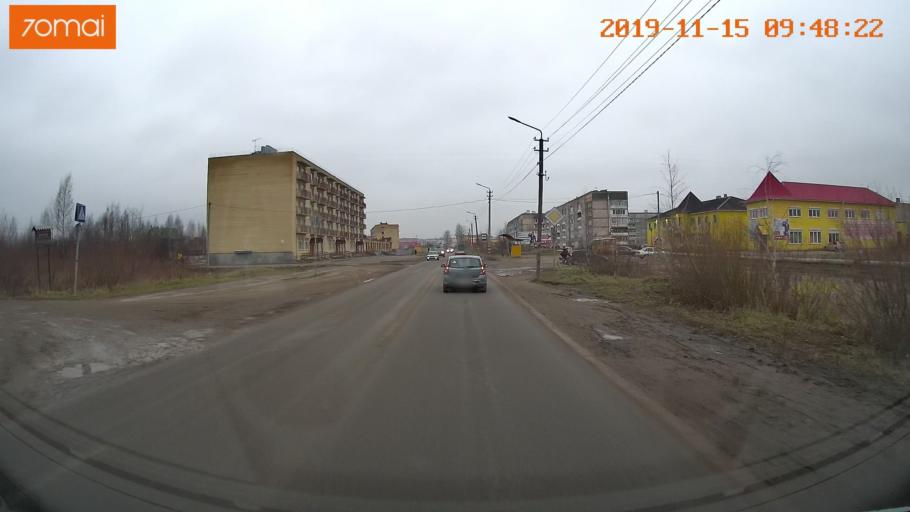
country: RU
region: Vologda
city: Sheksna
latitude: 59.2227
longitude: 38.5127
